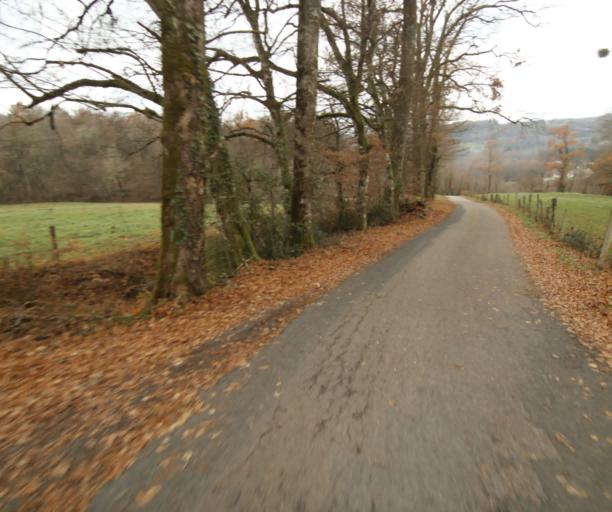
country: FR
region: Limousin
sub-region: Departement de la Correze
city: Sainte-Fortunade
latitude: 45.2340
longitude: 1.7422
